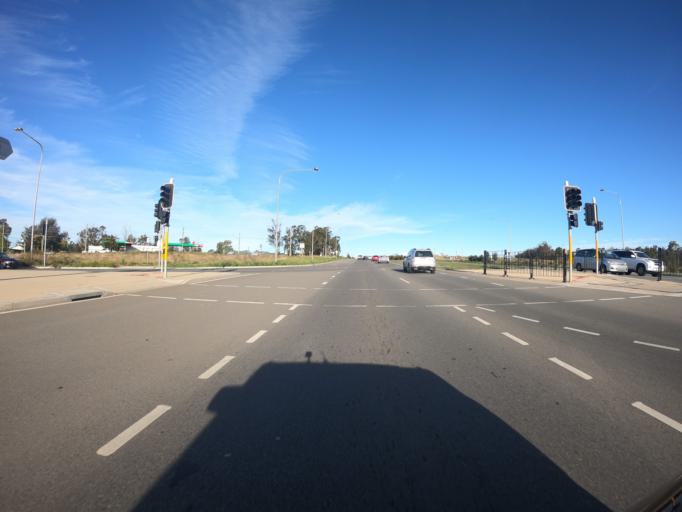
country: AU
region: New South Wales
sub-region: Blacktown
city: Hassall Grove
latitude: -33.6969
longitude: 150.8313
